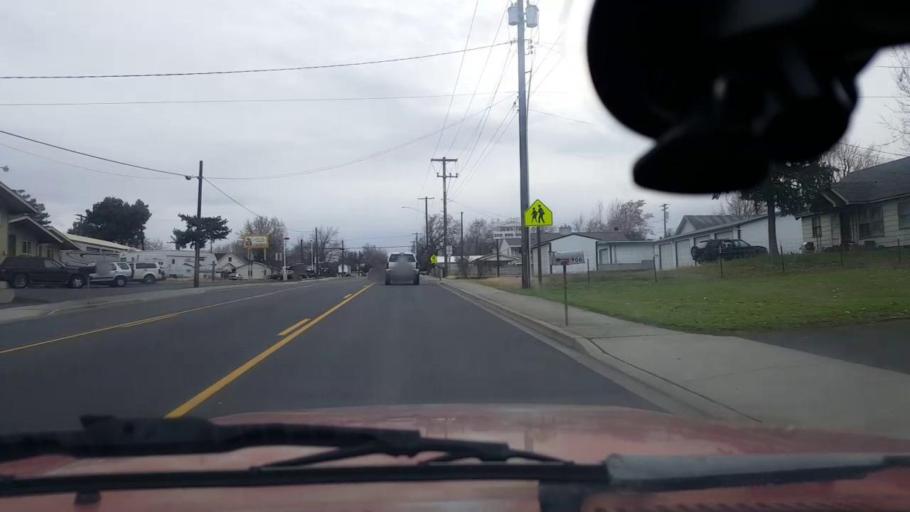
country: US
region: Washington
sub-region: Asotin County
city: West Clarkston-Highland
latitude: 46.4120
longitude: -117.0692
